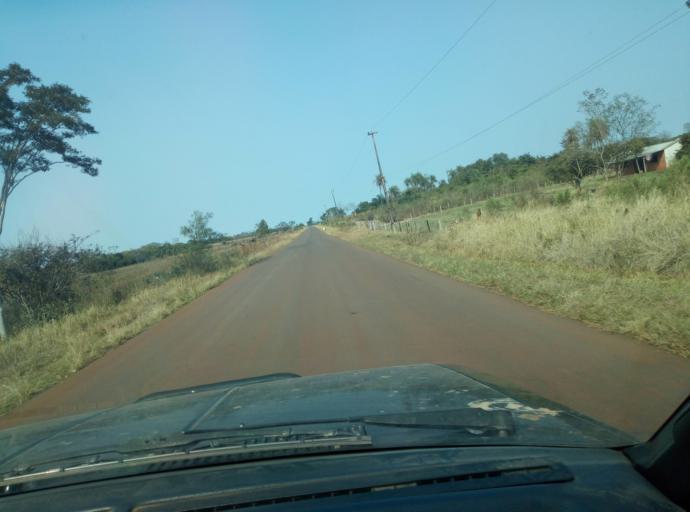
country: PY
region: Caaguazu
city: Carayao
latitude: -25.2247
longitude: -56.2891
